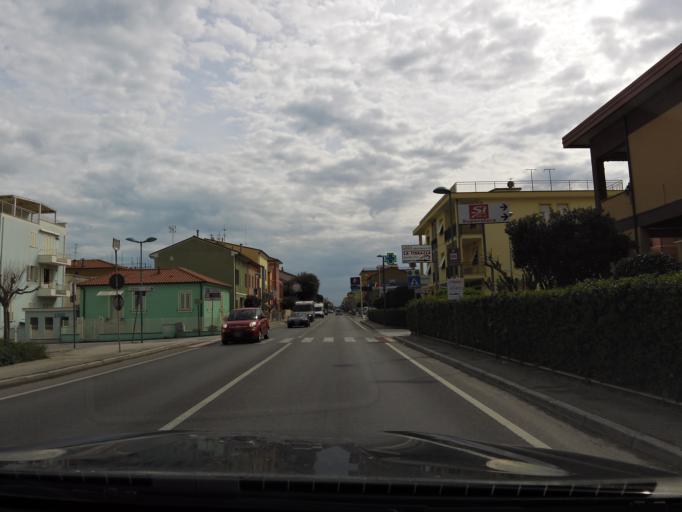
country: IT
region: The Marches
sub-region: Provincia di Macerata
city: Porto Potenza Picena
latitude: 43.3678
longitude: 13.6939
